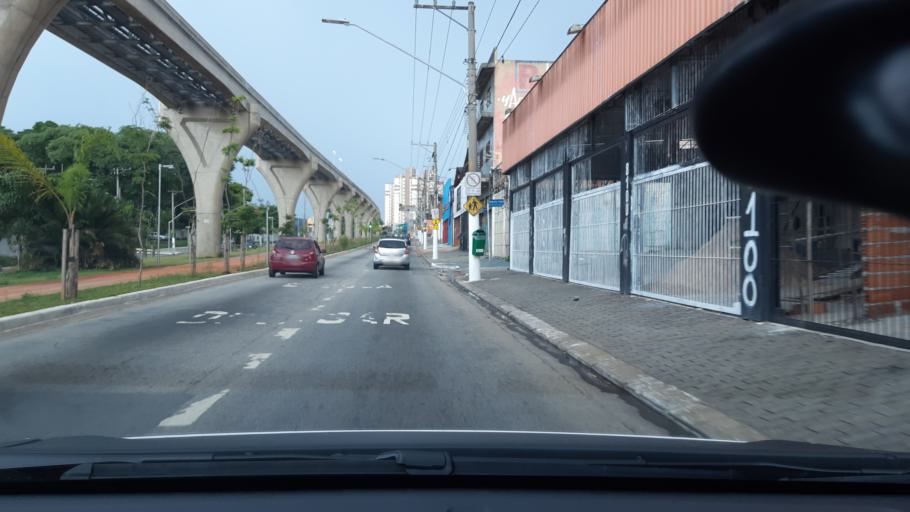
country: BR
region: Sao Paulo
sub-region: Sao Caetano Do Sul
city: Sao Caetano do Sul
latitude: -23.6022
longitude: -46.5237
